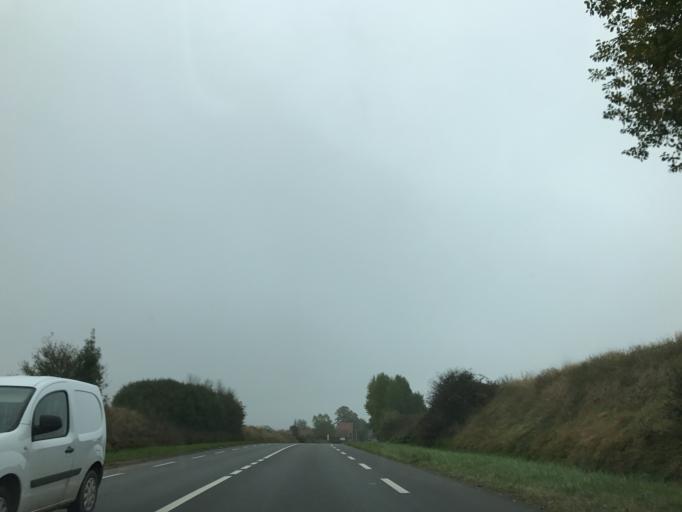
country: FR
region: Nord-Pas-de-Calais
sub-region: Departement du Pas-de-Calais
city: Beaurains
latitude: 50.2094
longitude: 2.8126
